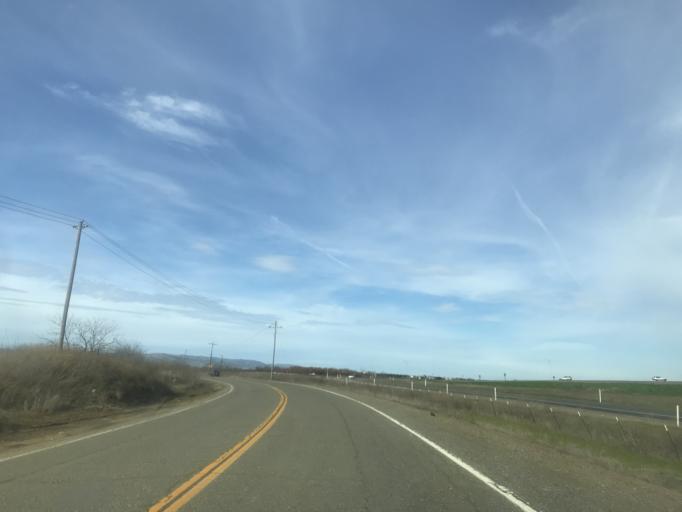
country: US
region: California
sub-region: Yolo County
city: Cottonwood
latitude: 38.6775
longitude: -121.9530
